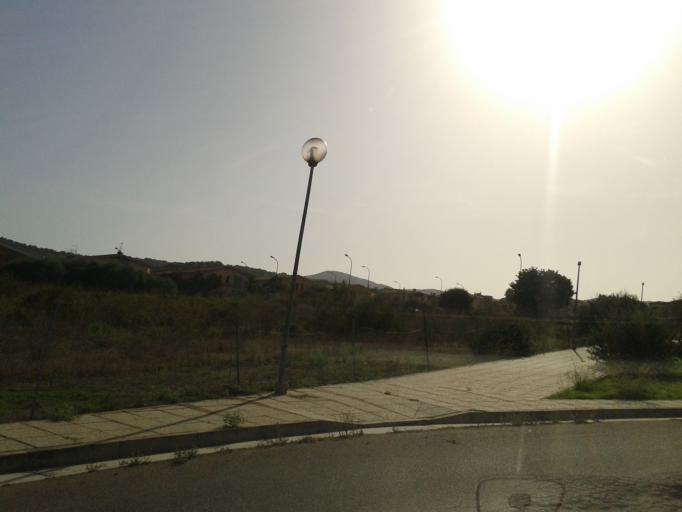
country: IT
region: Sardinia
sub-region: Provincia di Cagliari
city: Villasimius
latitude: 39.1508
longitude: 9.5149
